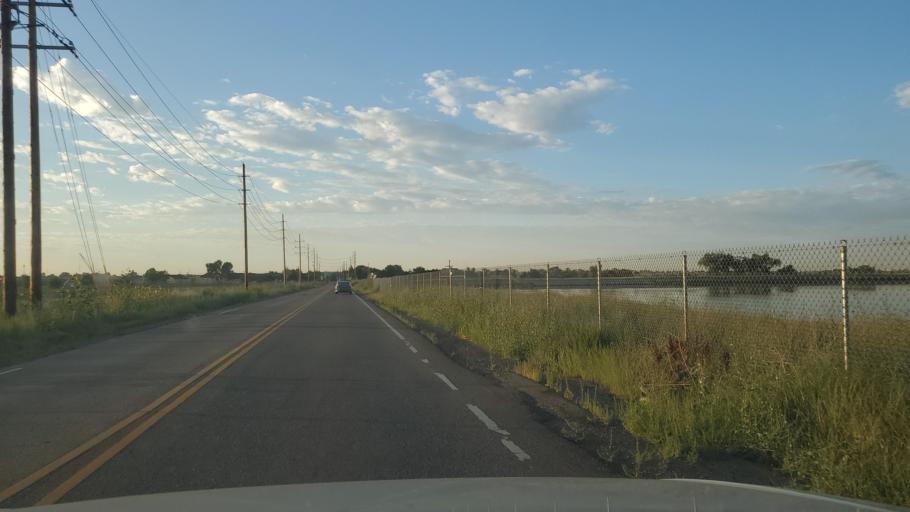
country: US
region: Colorado
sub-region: Adams County
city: Derby
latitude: 39.8774
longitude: -104.9154
